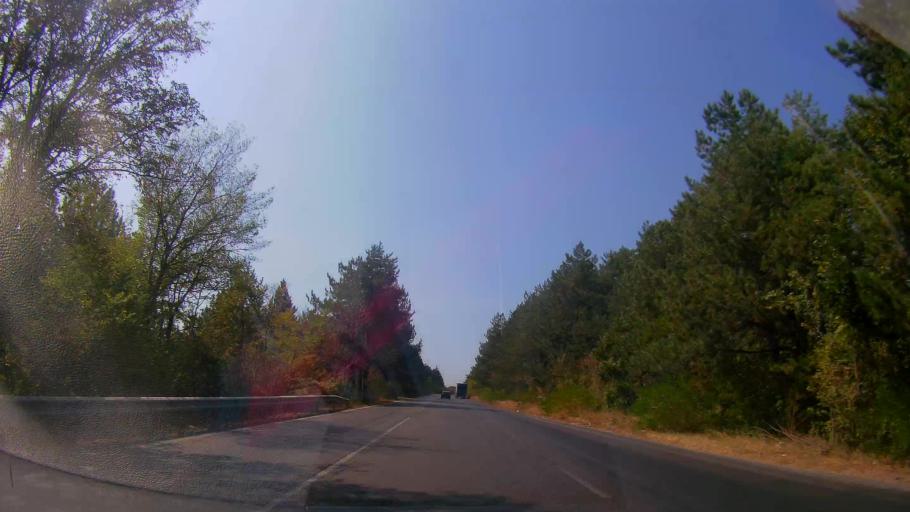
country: BG
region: Ruse
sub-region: Obshtina Vetovo
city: Senovo
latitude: 43.5611
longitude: 26.3767
